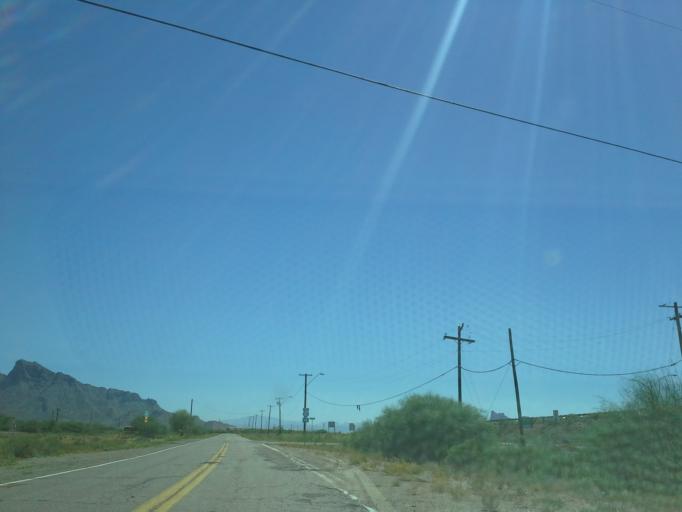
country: US
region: Arizona
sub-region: Pinal County
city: Eloy
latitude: 32.7146
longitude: -111.4990
